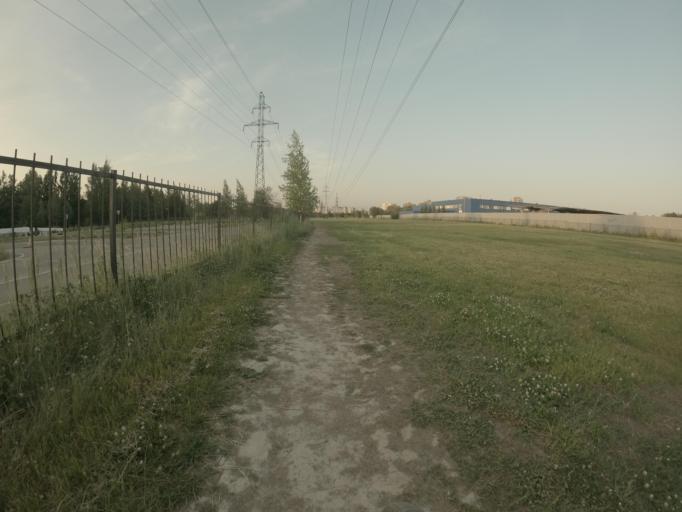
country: RU
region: St.-Petersburg
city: Krasnogvargeisky
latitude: 59.9414
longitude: 30.4528
